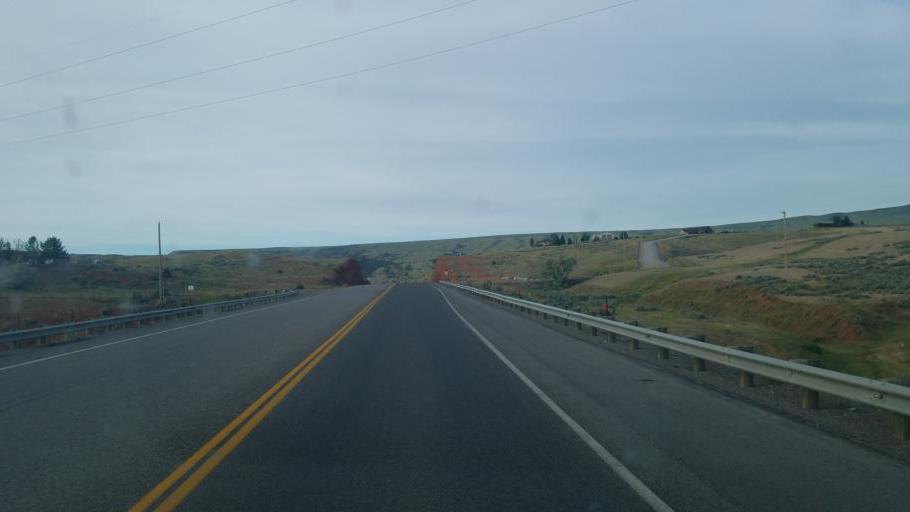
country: US
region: Wyoming
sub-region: Hot Springs County
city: Thermopolis
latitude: 43.6048
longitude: -108.2157
